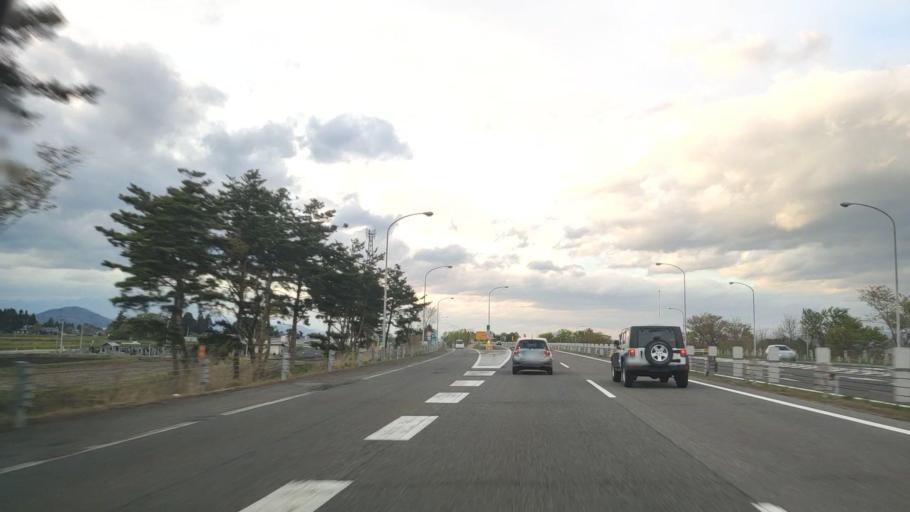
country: JP
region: Iwate
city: Morioka-shi
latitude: 39.6152
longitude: 141.1297
